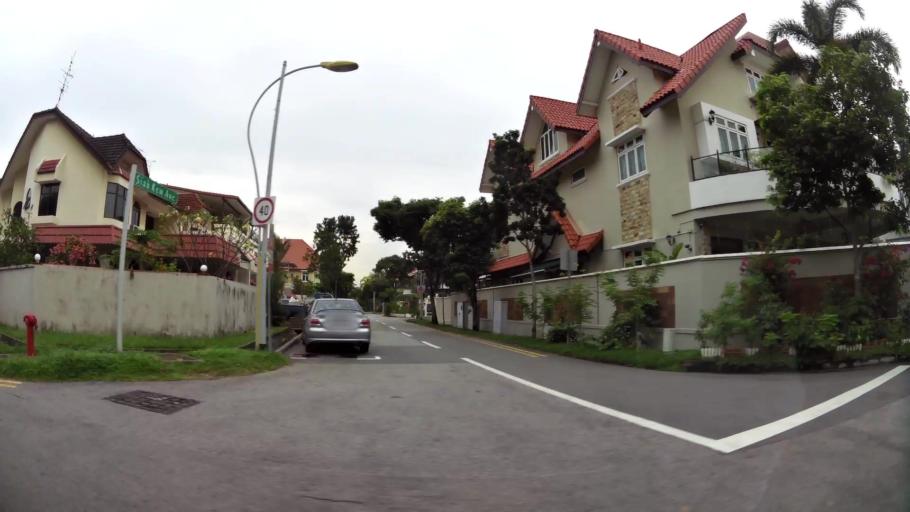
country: SG
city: Singapore
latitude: 1.3297
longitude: 103.8702
